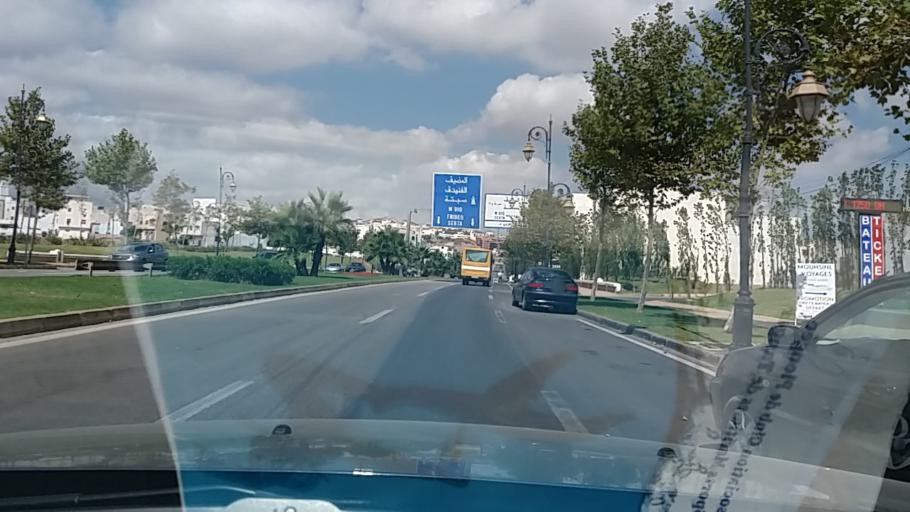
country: MA
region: Tanger-Tetouan
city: Tetouan
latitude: 35.5926
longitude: -5.3363
